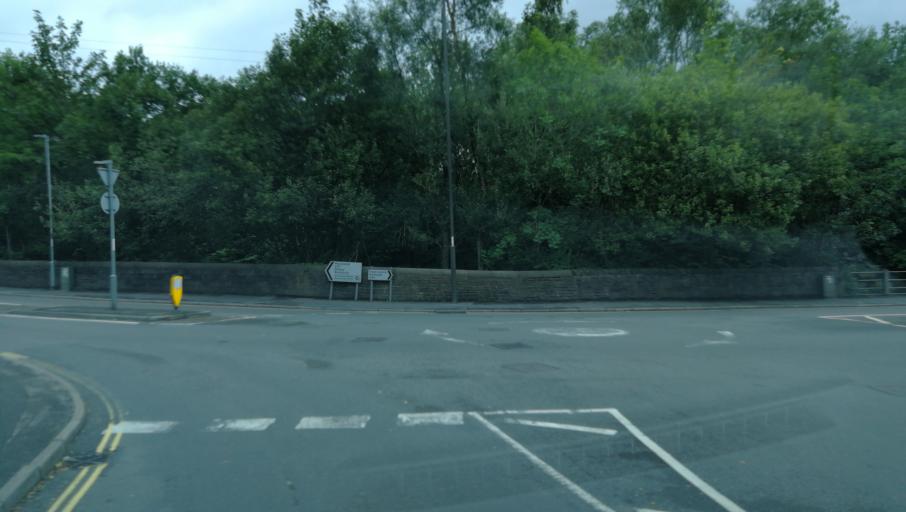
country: GB
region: England
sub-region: Derbyshire
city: Glossop
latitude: 53.4441
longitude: -1.9666
